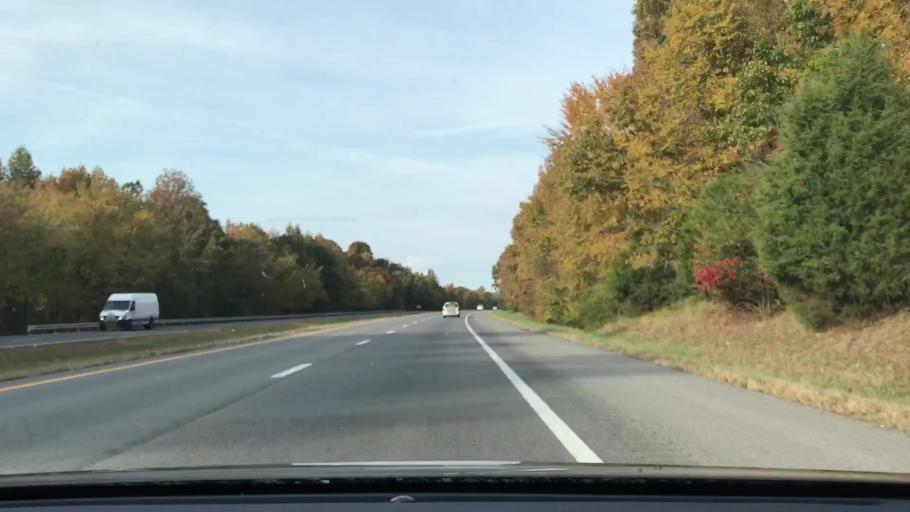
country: US
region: Kentucky
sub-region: Graves County
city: Mayfield
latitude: 36.7705
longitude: -88.6119
